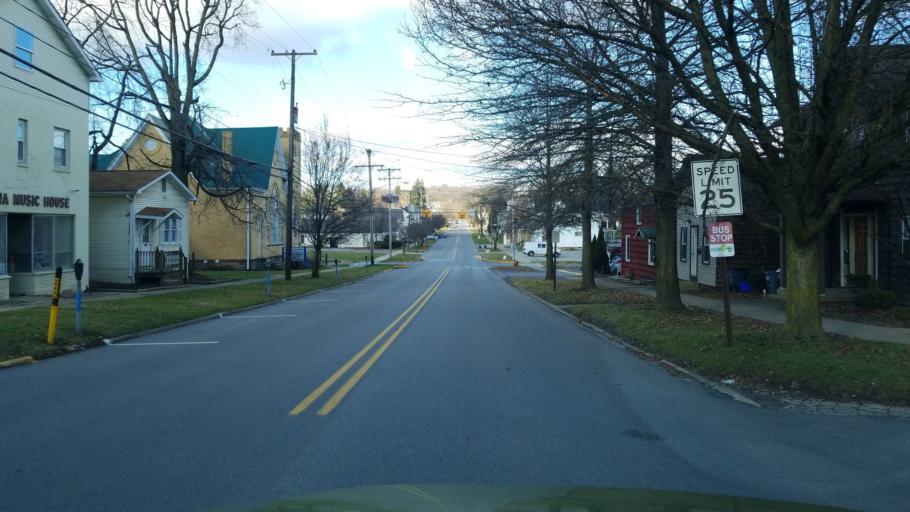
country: US
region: Pennsylvania
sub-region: Indiana County
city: Indiana
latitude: 40.6236
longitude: -79.1482
